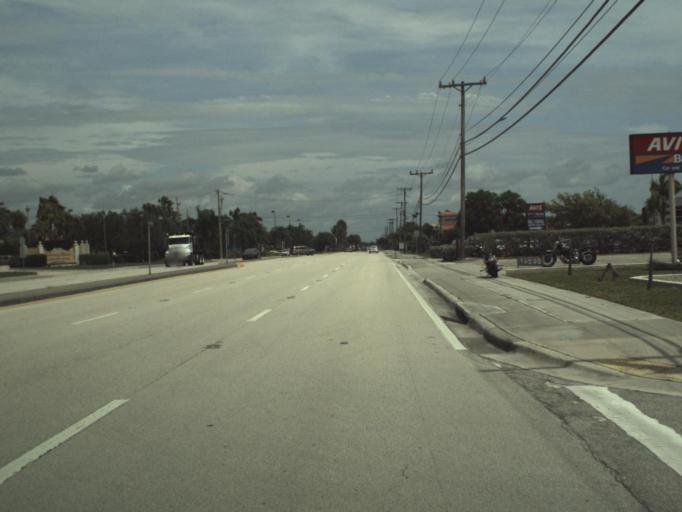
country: US
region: Florida
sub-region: Palm Beach County
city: Jupiter
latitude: 26.9641
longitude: -80.0850
